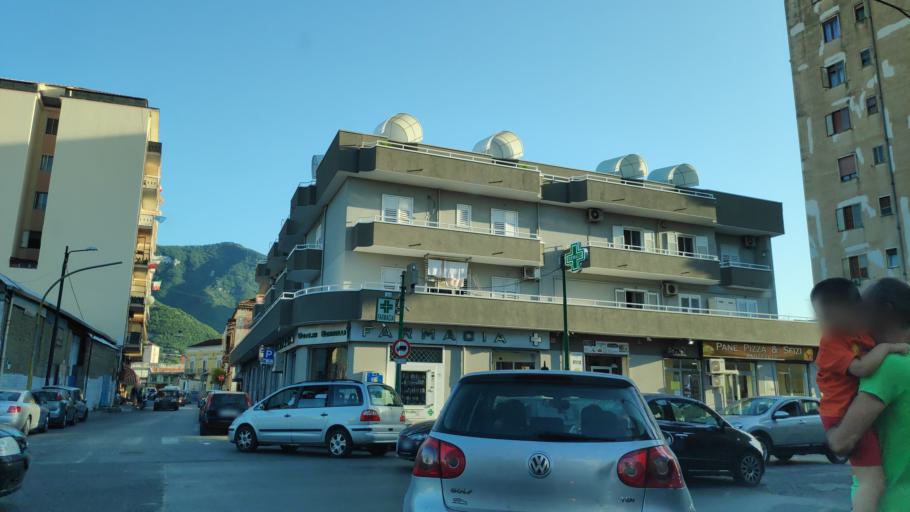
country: IT
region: Campania
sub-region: Provincia di Salerno
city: Pagani
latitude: 40.7486
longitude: 14.6147
